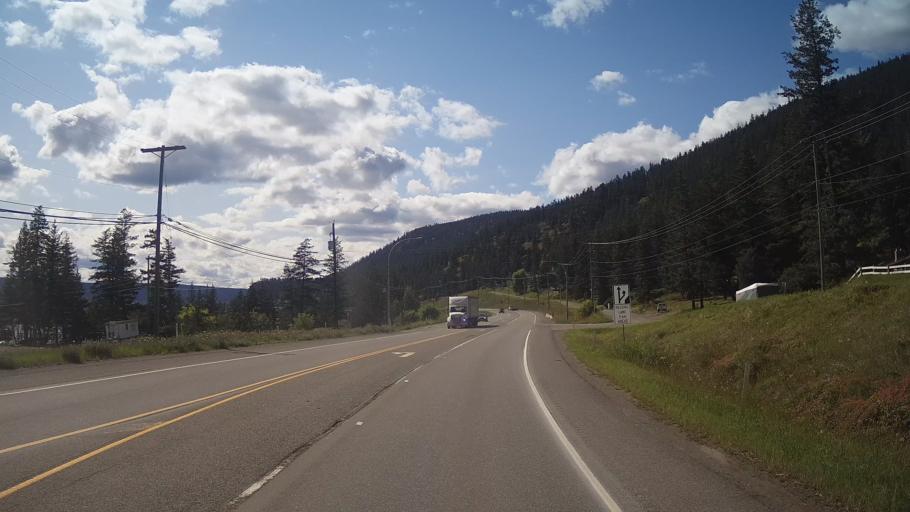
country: CA
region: British Columbia
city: Williams Lake
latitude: 52.1235
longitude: -122.0654
